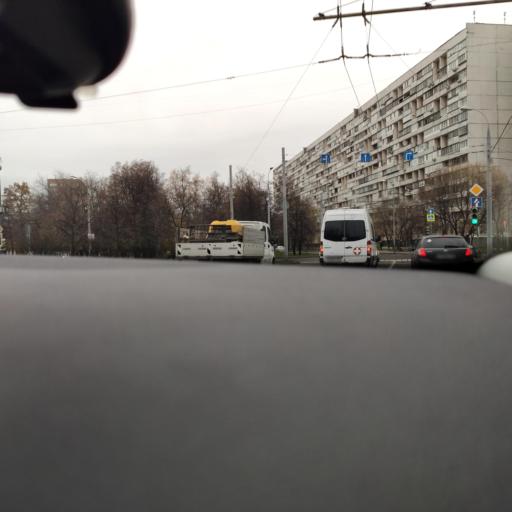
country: RU
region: Moscow
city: Novyye Kuz'minki
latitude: 55.6938
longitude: 37.7558
